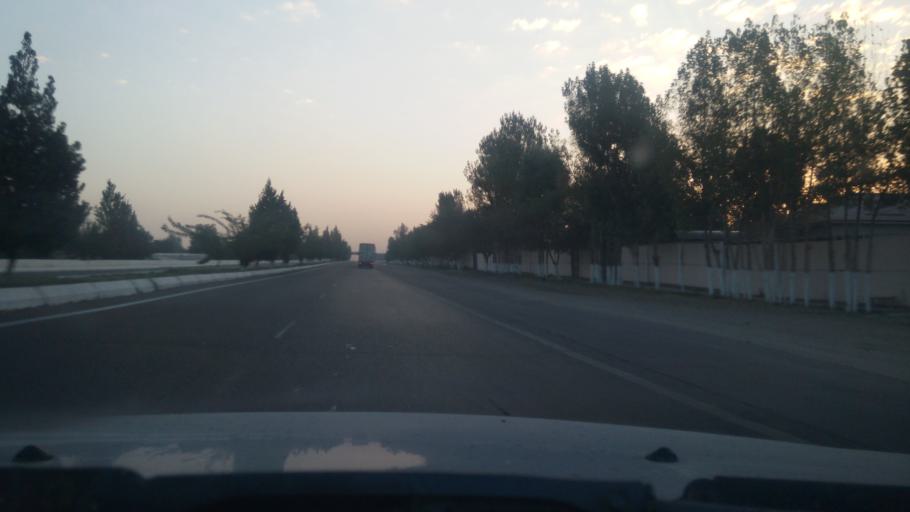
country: UZ
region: Toshkent
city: Zafar
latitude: 41.0083
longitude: 68.8345
